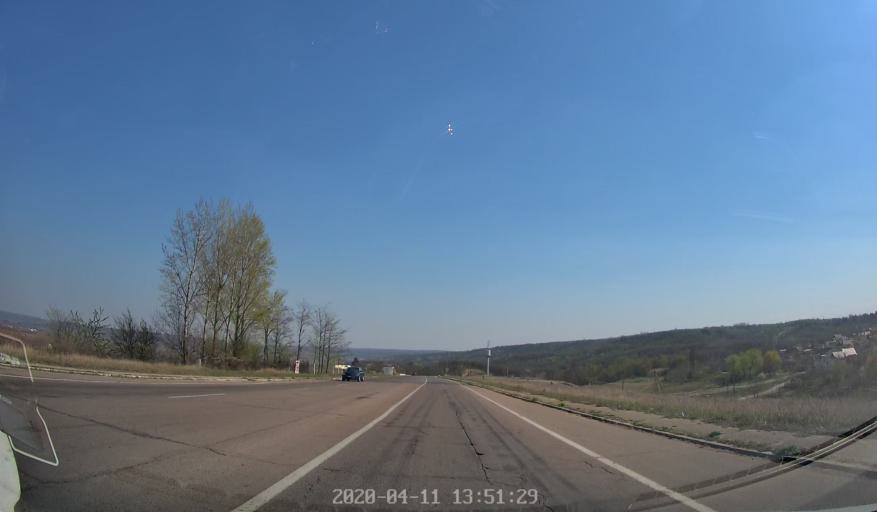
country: MD
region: Chisinau
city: Vadul lui Voda
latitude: 47.0862
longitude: 29.0746
